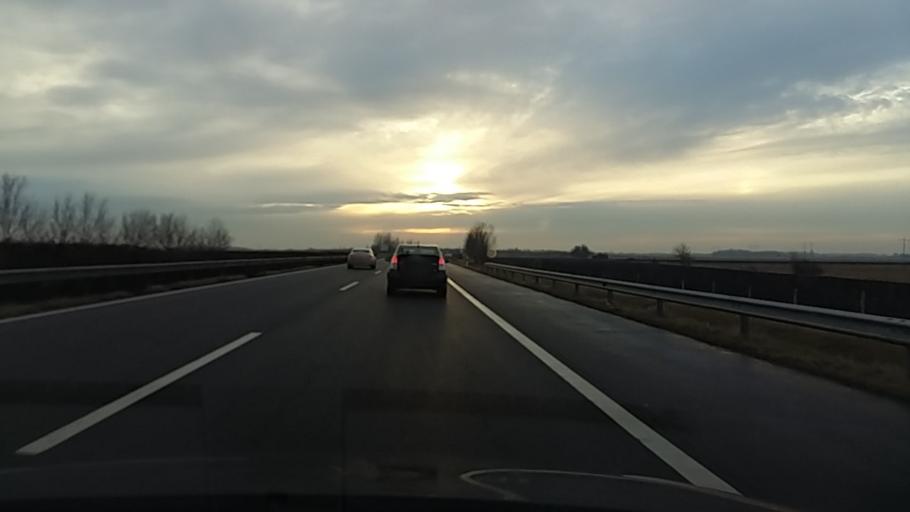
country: HU
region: Borsod-Abauj-Zemplen
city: Mezokeresztes
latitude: 47.8196
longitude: 20.7236
